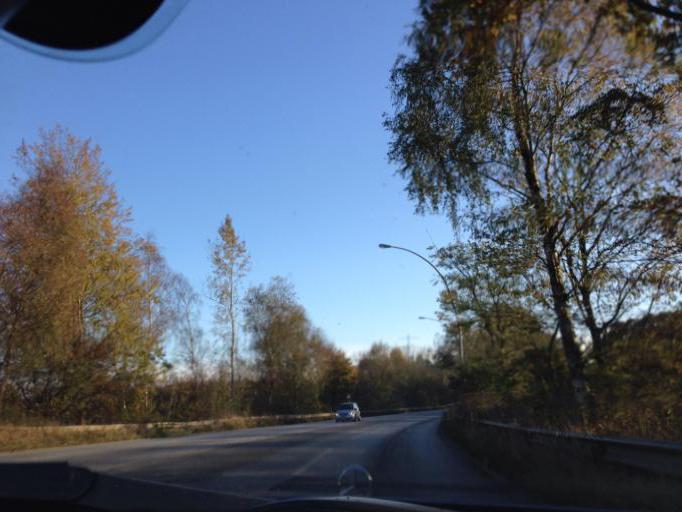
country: DE
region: Schleswig-Holstein
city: Stapelfeld
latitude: 53.6140
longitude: 10.1755
